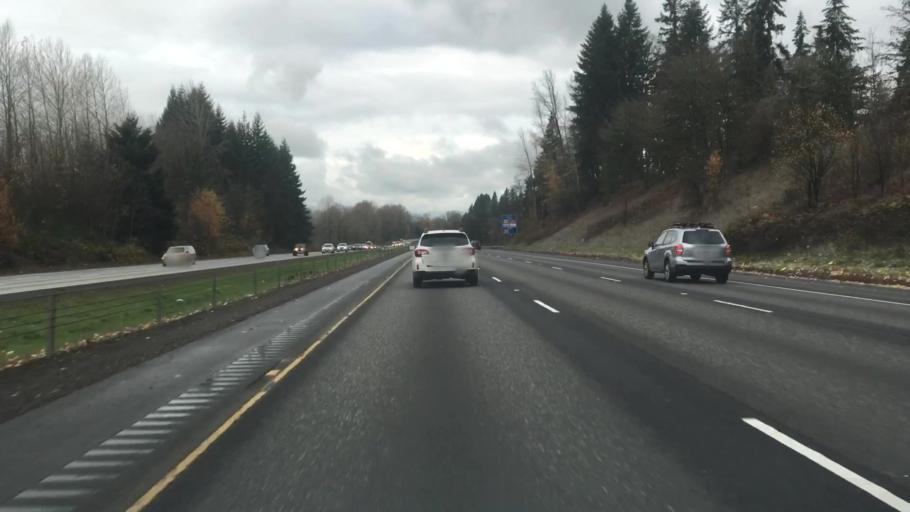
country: US
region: Washington
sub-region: Cowlitz County
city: Woodland
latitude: 45.8802
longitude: -122.7212
